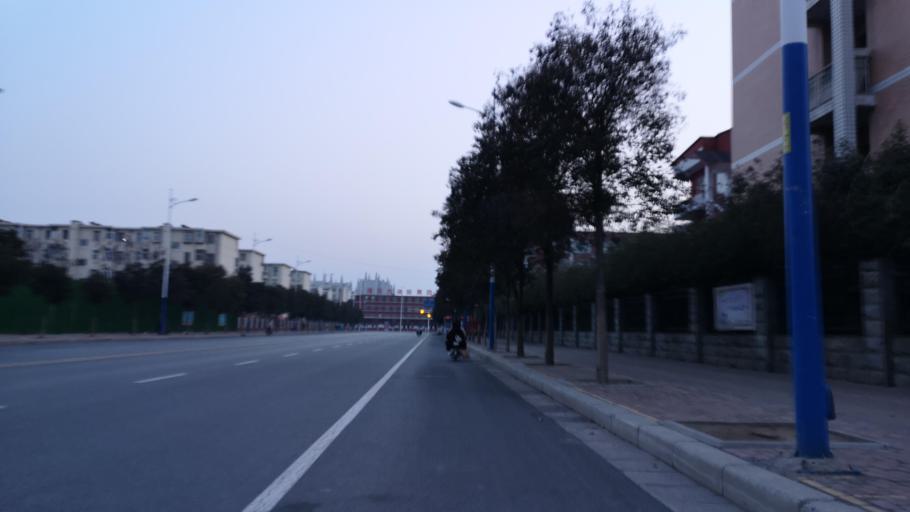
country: CN
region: Henan Sheng
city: Zhongyuanlu
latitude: 35.7653
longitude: 115.0627
